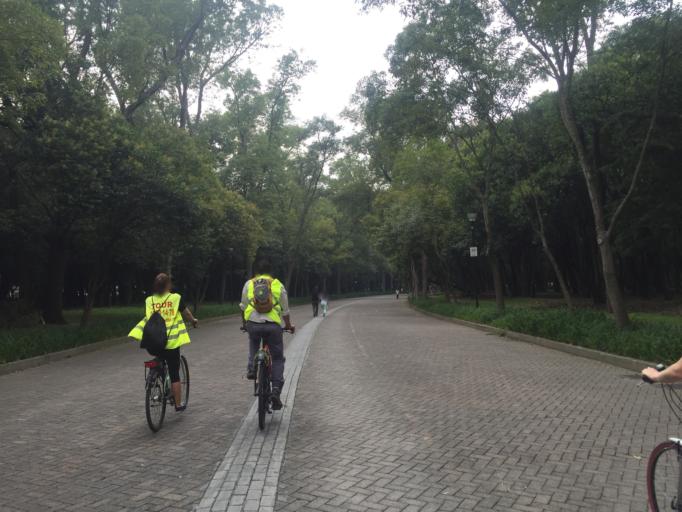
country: MX
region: Mexico City
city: Polanco
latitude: 19.4168
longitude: -99.1836
